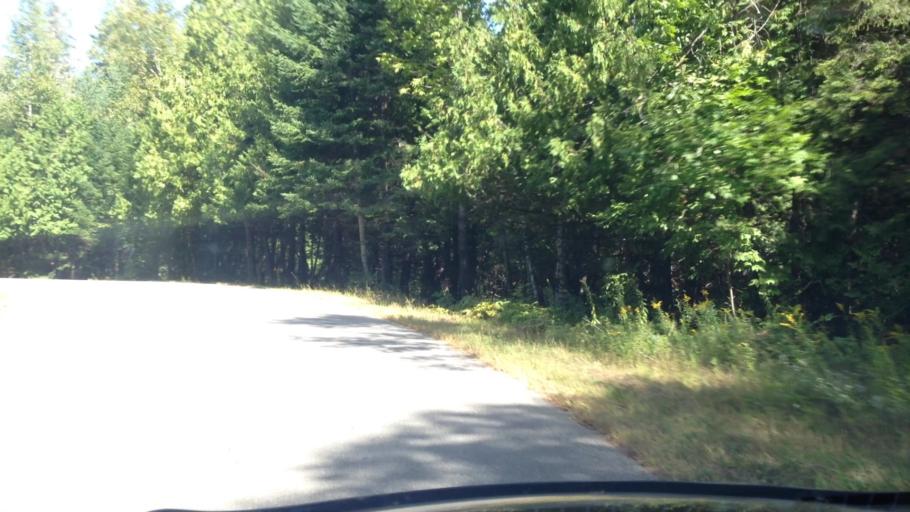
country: CA
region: Quebec
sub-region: Laurentides
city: Mont-Tremblant
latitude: 45.9417
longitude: -74.5871
